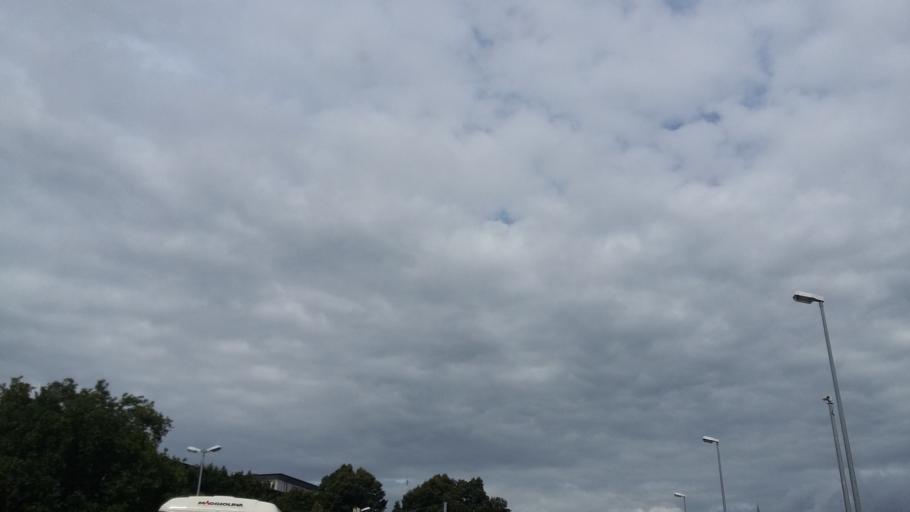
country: DE
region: Lower Saxony
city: Hannover
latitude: 52.3665
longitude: 9.7268
